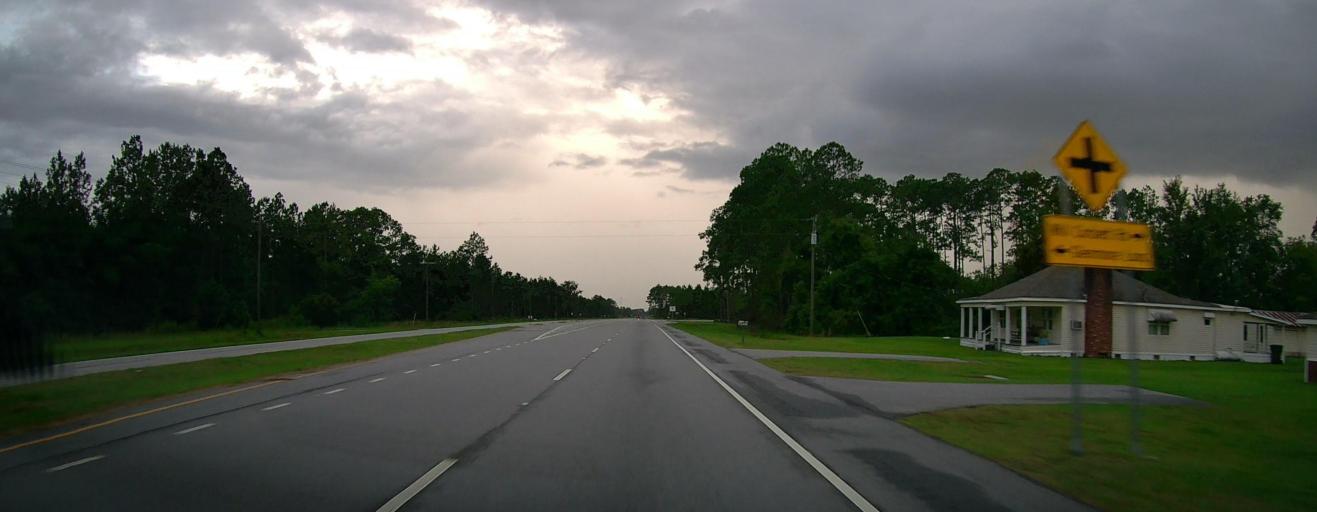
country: US
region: Georgia
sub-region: Ware County
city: Deenwood
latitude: 31.1256
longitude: -82.5257
